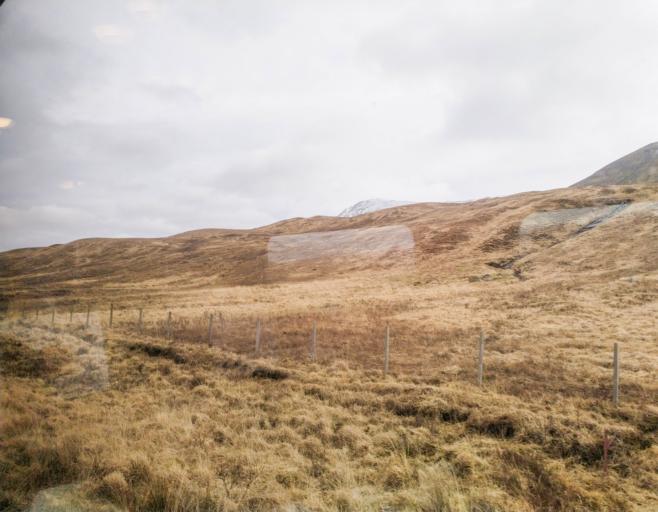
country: GB
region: Scotland
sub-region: Highland
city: Spean Bridge
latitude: 56.5388
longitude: -4.7606
